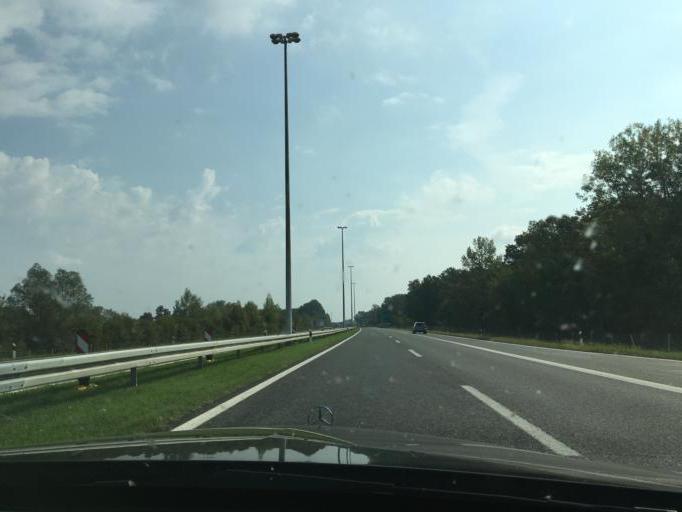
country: HR
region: Brodsko-Posavska
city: Garcin
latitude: 45.1477
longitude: 18.2776
